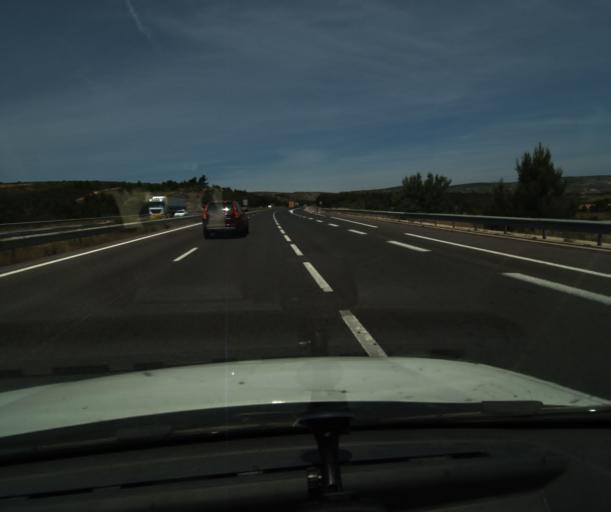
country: FR
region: Languedoc-Roussillon
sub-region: Departement des Pyrenees-Orientales
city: Salses-le-Chateau
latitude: 42.8365
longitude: 2.9101
